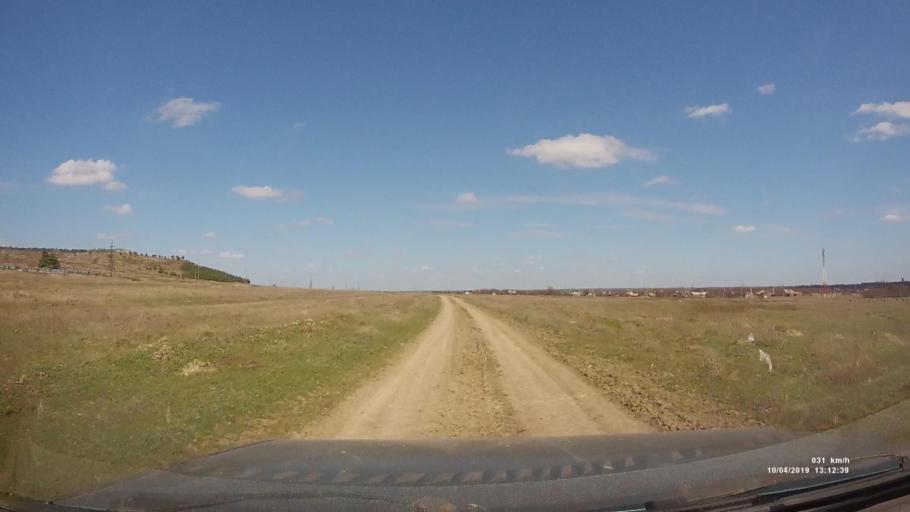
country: RU
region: Rostov
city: Masalovka
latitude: 48.4137
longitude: 40.2564
